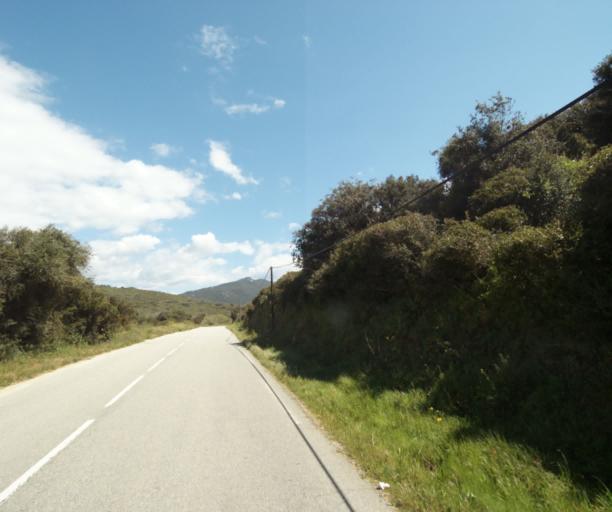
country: FR
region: Corsica
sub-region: Departement de la Corse-du-Sud
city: Propriano
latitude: 41.6582
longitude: 8.8976
